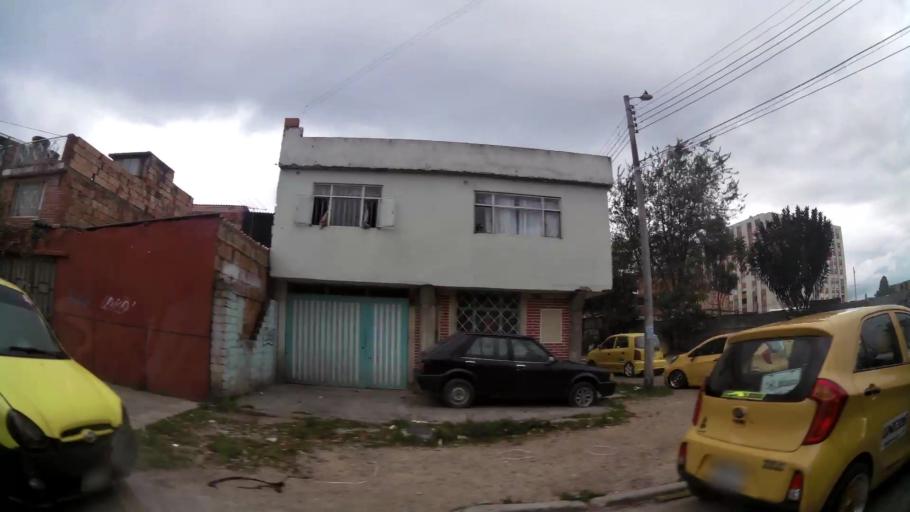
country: CO
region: Bogota D.C.
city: Barrio San Luis
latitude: 4.6986
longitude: -74.1077
